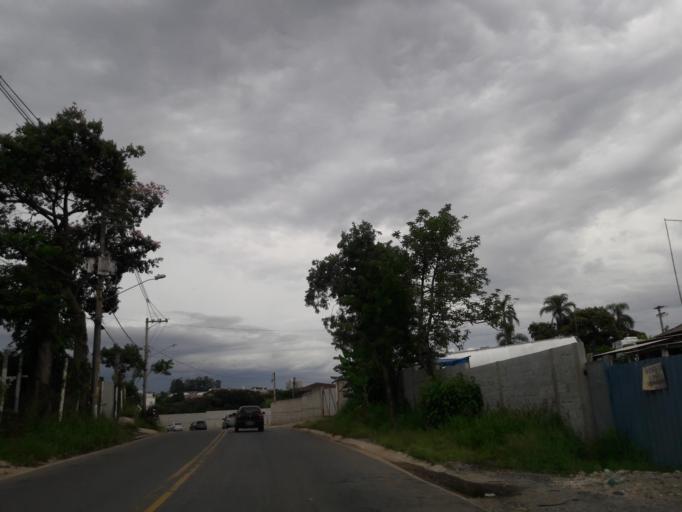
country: BR
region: Sao Paulo
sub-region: Aruja
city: Aruja
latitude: -23.3994
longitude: -46.4073
